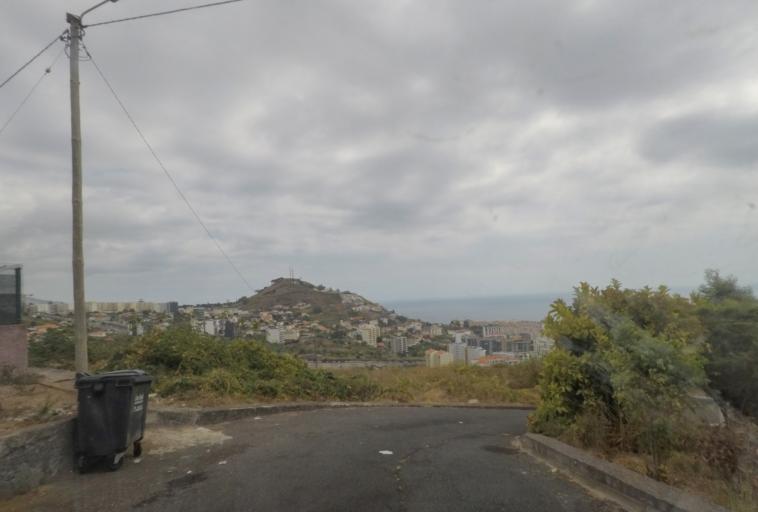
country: PT
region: Madeira
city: Camara de Lobos
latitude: 32.6468
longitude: -16.9498
